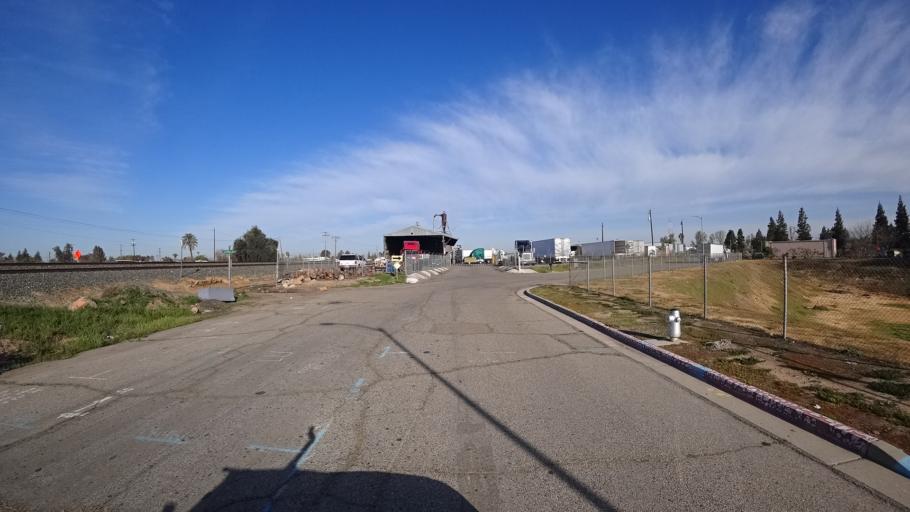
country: US
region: California
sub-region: Fresno County
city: West Park
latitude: 36.8112
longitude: -119.8803
